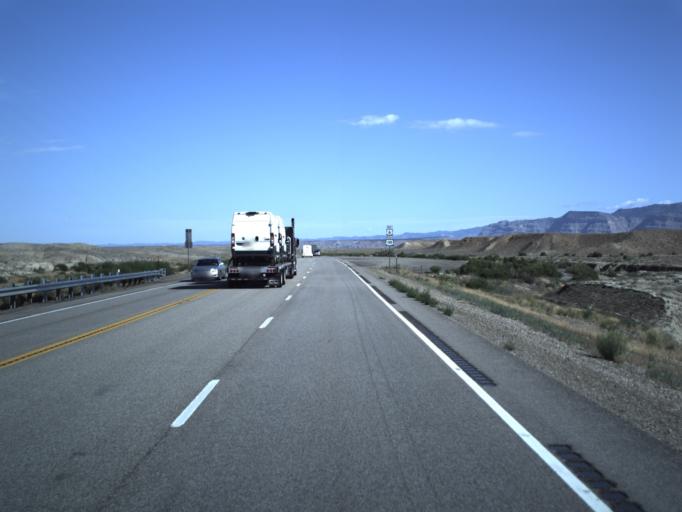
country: US
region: Utah
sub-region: Carbon County
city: East Carbon City
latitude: 39.2906
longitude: -110.3525
